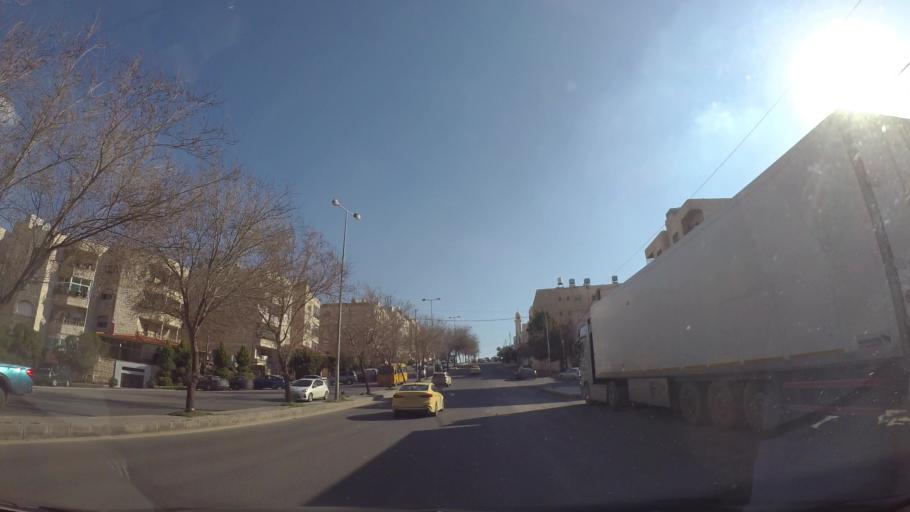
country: JO
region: Amman
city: Amman
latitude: 31.9755
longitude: 35.9387
